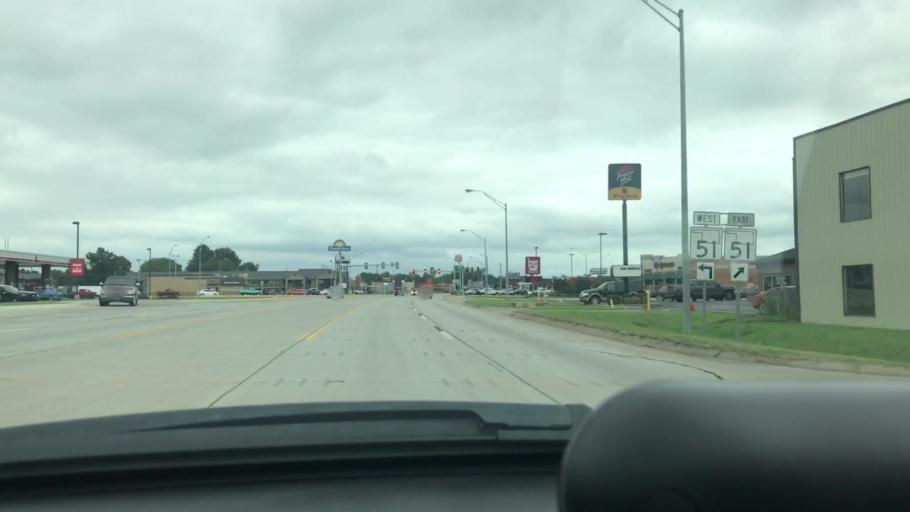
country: US
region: Oklahoma
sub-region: Wagoner County
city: Wagoner
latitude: 35.9576
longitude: -95.3951
